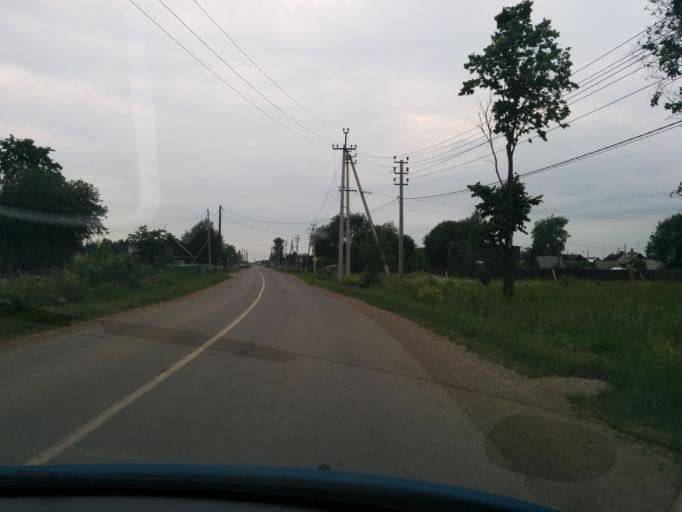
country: RU
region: Perm
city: Polazna
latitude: 58.2326
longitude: 56.2884
